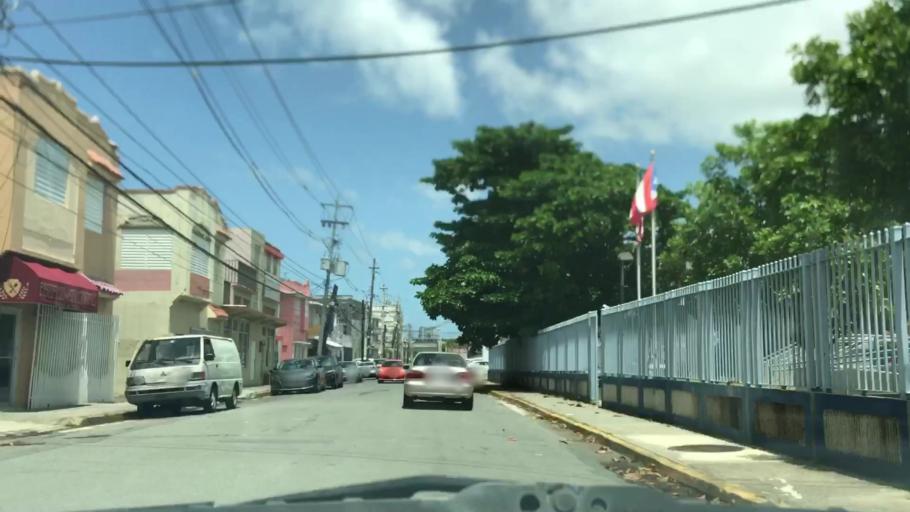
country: PR
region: Catano
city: Catano
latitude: 18.4203
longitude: -66.0618
